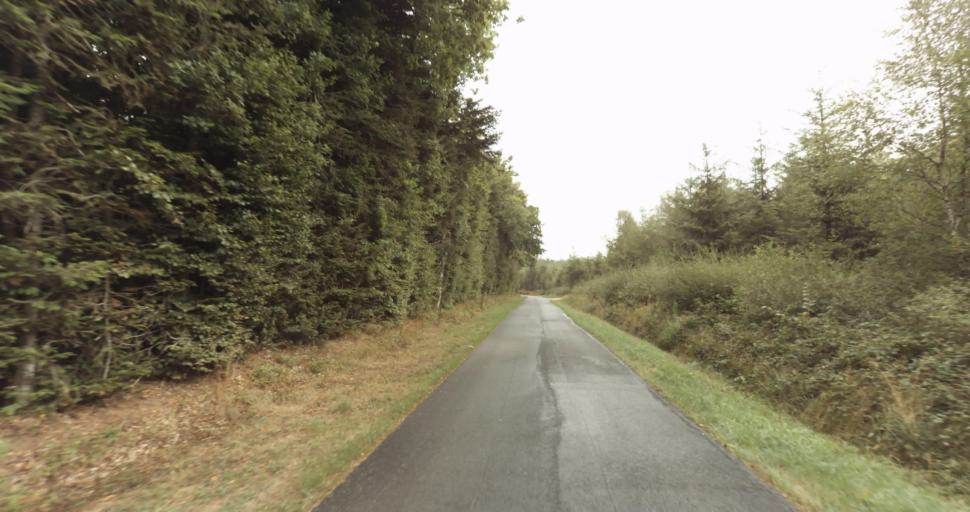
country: FR
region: Lower Normandy
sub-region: Departement de l'Orne
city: Gace
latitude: 48.8177
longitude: 0.3402
